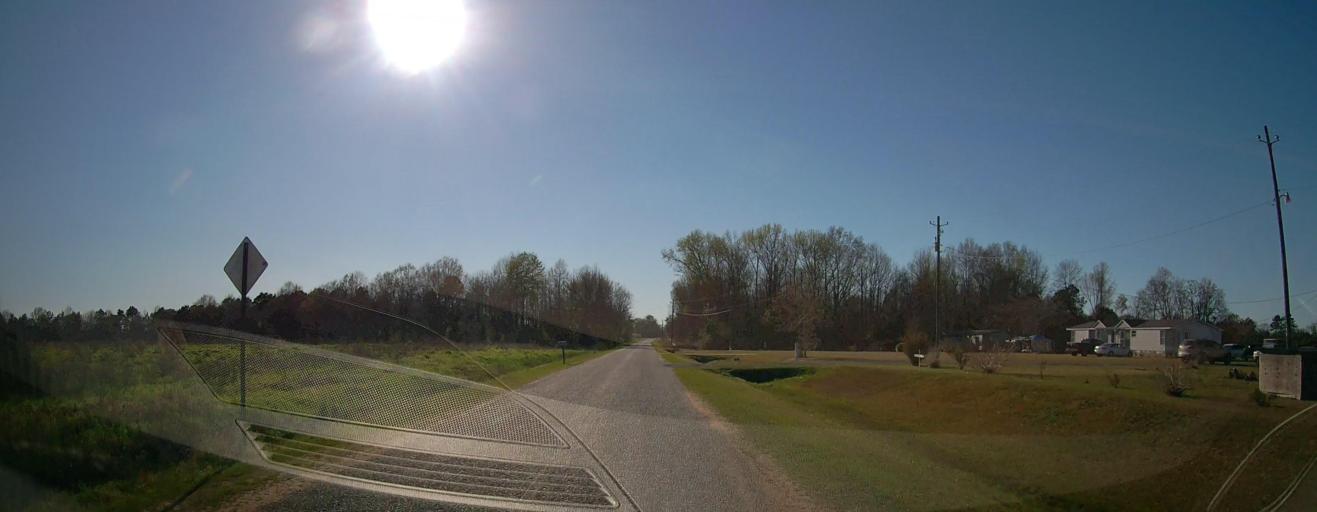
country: US
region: Georgia
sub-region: Taylor County
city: Reynolds
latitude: 32.5550
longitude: -84.0790
